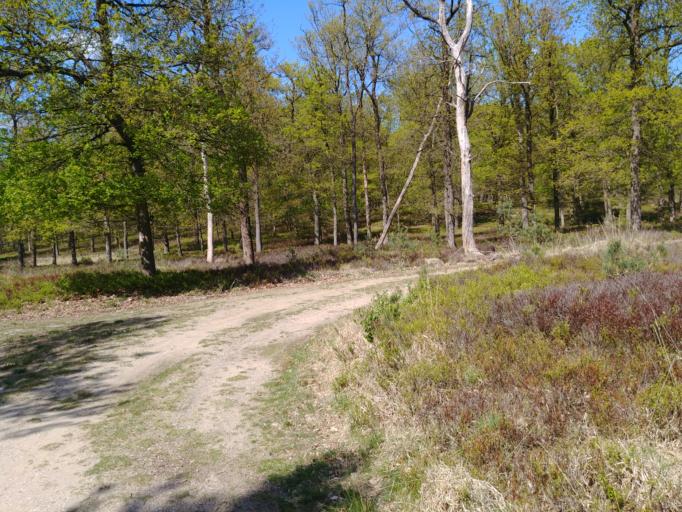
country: NL
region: Gelderland
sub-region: Gemeente Apeldoorn
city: Uddel
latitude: 52.2441
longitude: 5.8621
